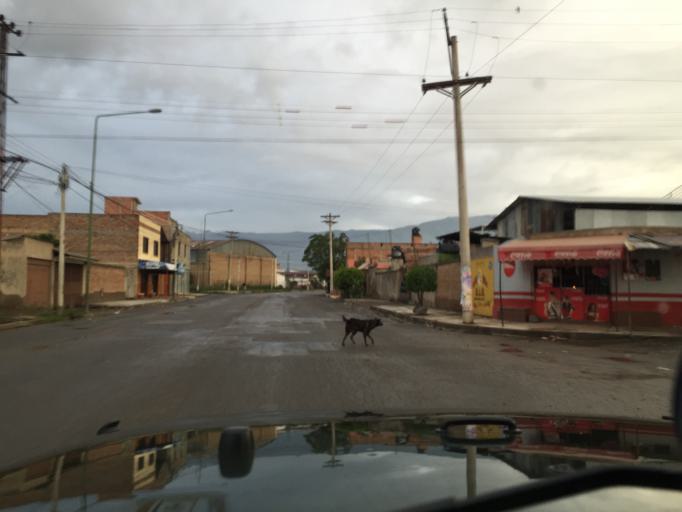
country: BO
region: Cochabamba
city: Cochabamba
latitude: -17.4158
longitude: -66.1685
